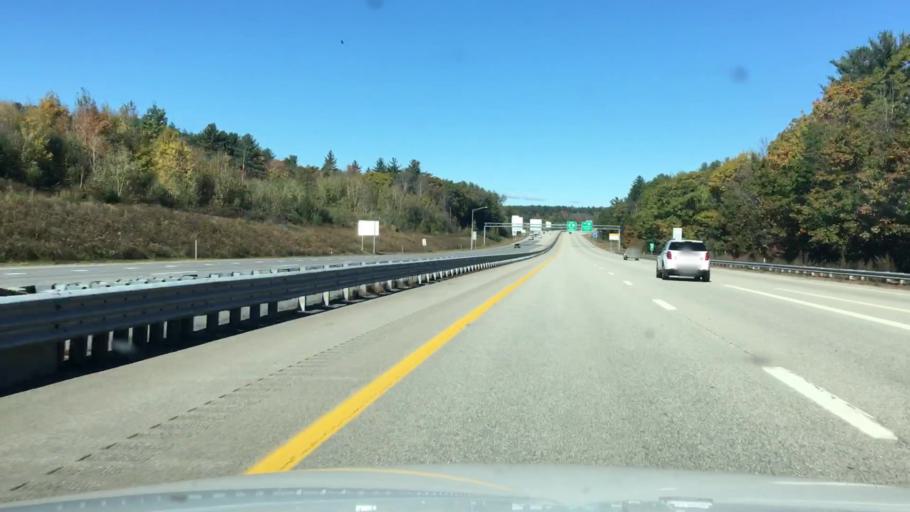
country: US
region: New Hampshire
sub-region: Strafford County
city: Rochester
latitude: 43.2861
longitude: -70.9851
